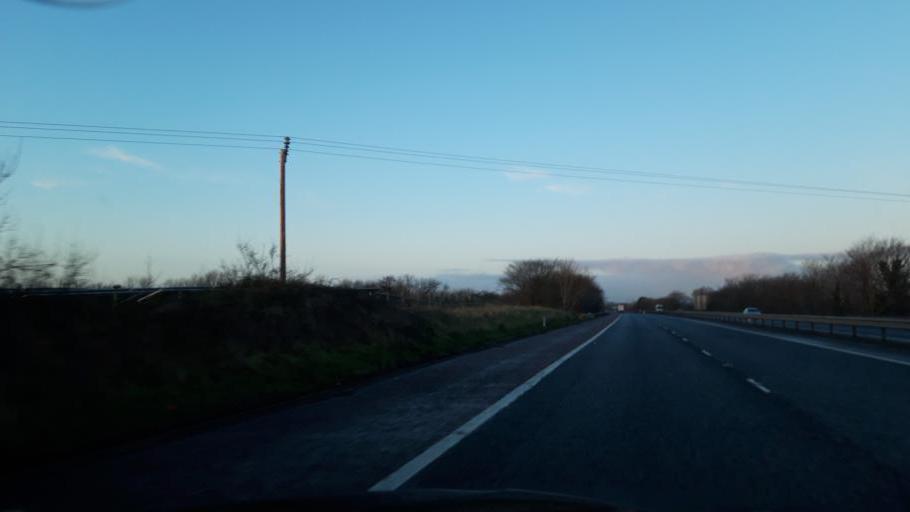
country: GB
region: Northern Ireland
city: Randalstown
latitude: 54.7443
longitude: -6.2529
